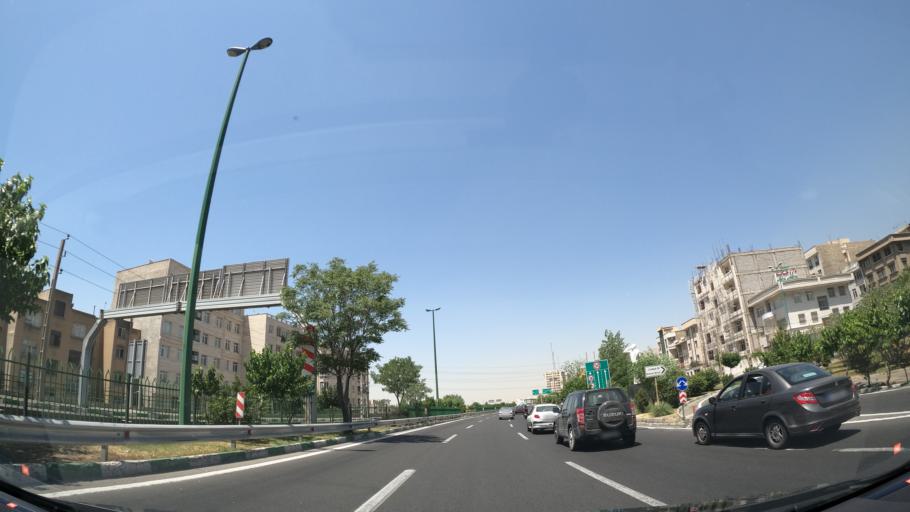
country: IR
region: Tehran
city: Tajrish
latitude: 35.7638
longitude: 51.3018
